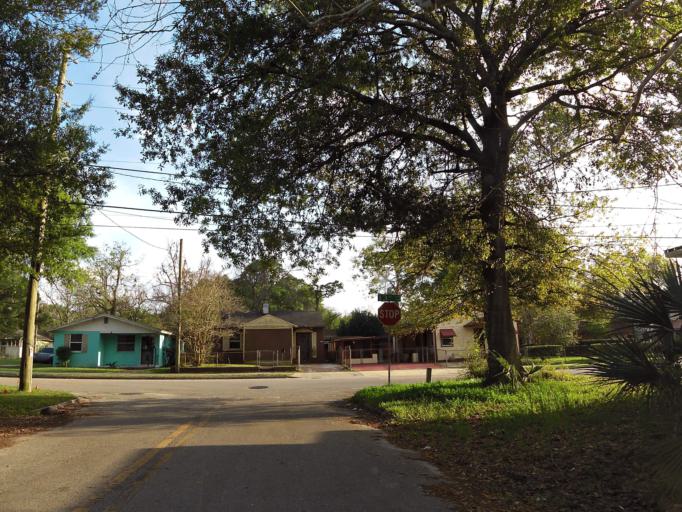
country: US
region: Florida
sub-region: Duval County
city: Jacksonville
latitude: 30.3516
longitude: -81.6810
